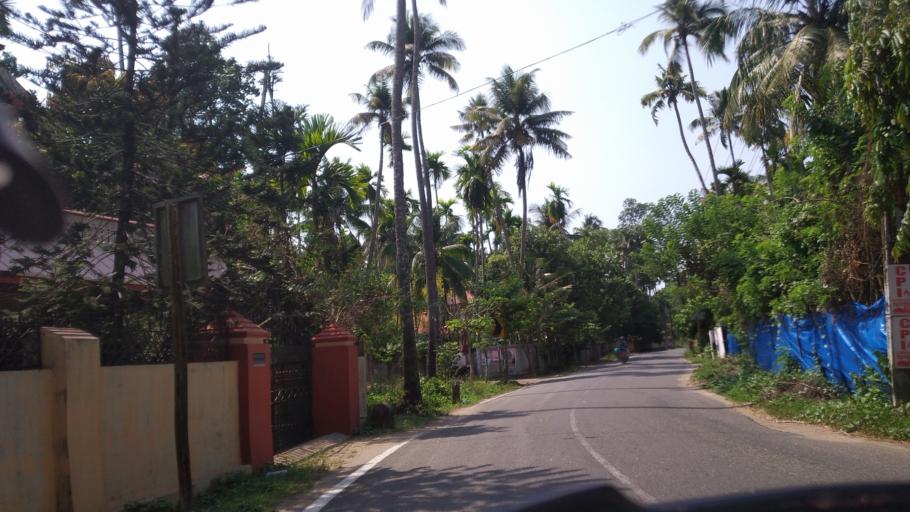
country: IN
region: Kerala
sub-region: Thrissur District
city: Irinjalakuda
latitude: 10.3018
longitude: 76.1308
